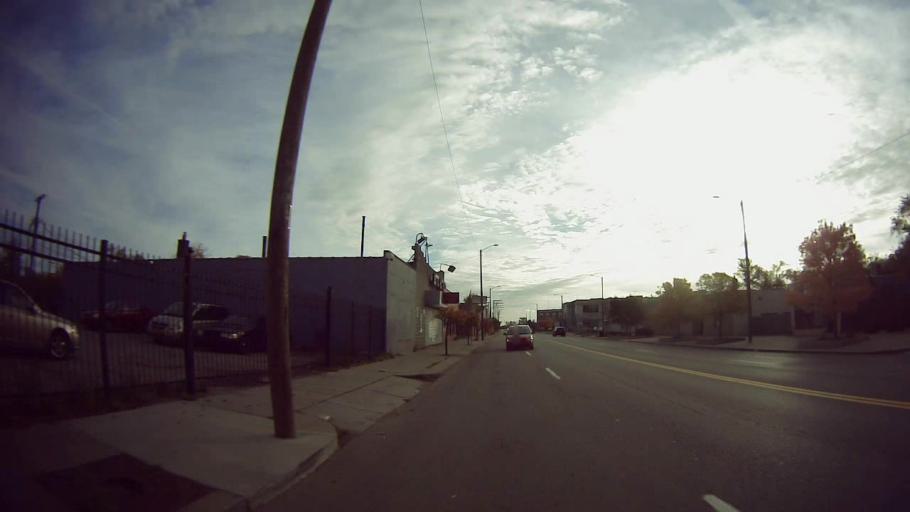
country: US
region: Michigan
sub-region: Wayne County
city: Highland Park
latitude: 42.4323
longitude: -83.1059
